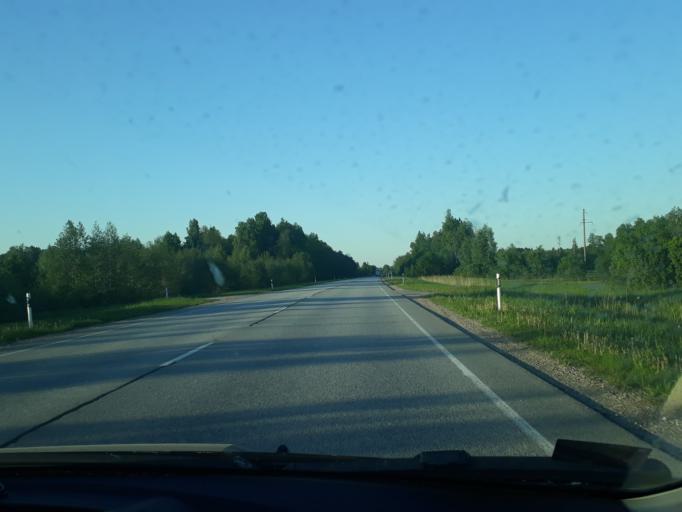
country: EE
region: Paernumaa
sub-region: Sindi linn
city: Sindi
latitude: 58.4685
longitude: 24.7098
